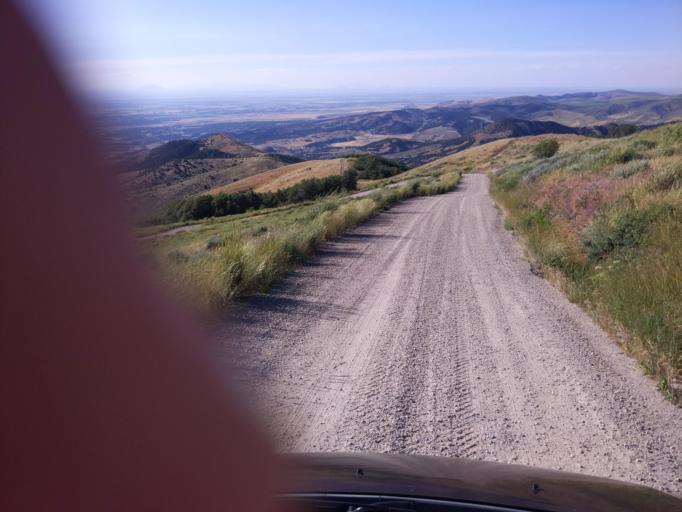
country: US
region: Idaho
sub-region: Bannock County
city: Pocatello
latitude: 42.8507
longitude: -112.3623
